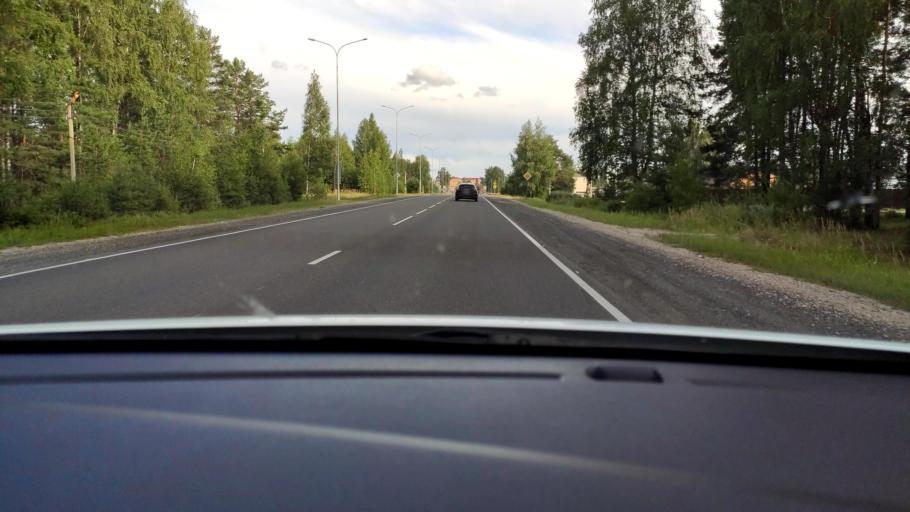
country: RU
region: Mariy-El
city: Suslonger
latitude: 56.3856
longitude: 48.1928
